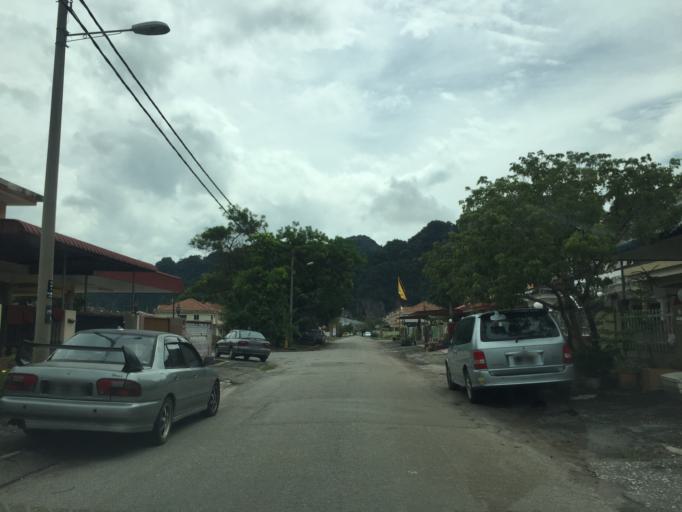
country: MY
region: Perak
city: Ipoh
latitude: 4.5656
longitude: 101.1209
